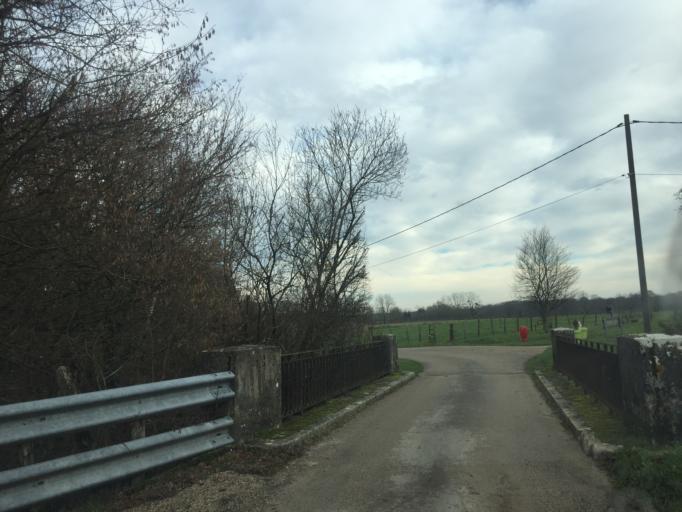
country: FR
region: Franche-Comte
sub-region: Departement du Jura
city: Chaussin
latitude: 46.9096
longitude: 5.4655
